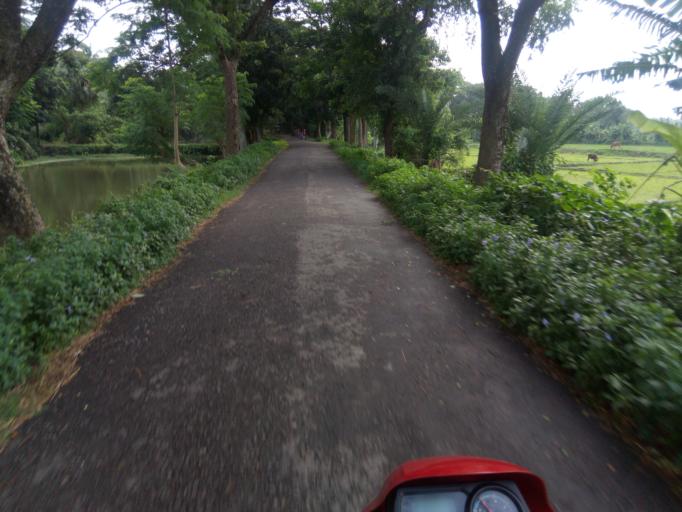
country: BD
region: Khulna
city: Kalia
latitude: 22.9570
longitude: 89.5530
